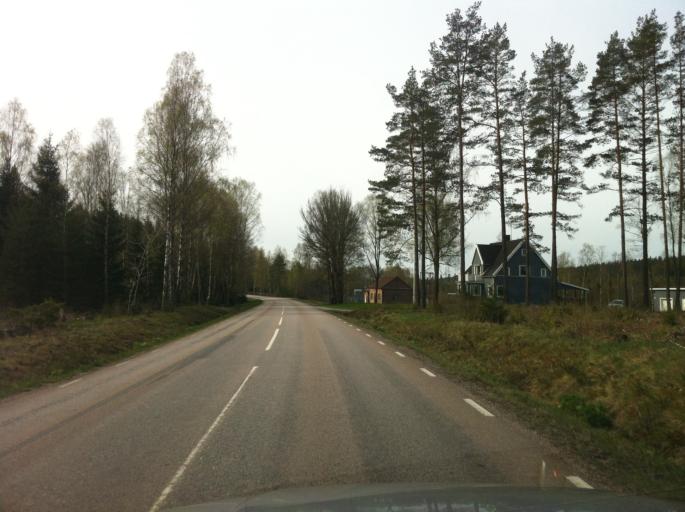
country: SE
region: Vaestra Goetaland
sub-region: Bollebygds Kommun
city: Bollebygd
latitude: 57.7230
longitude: 12.5855
